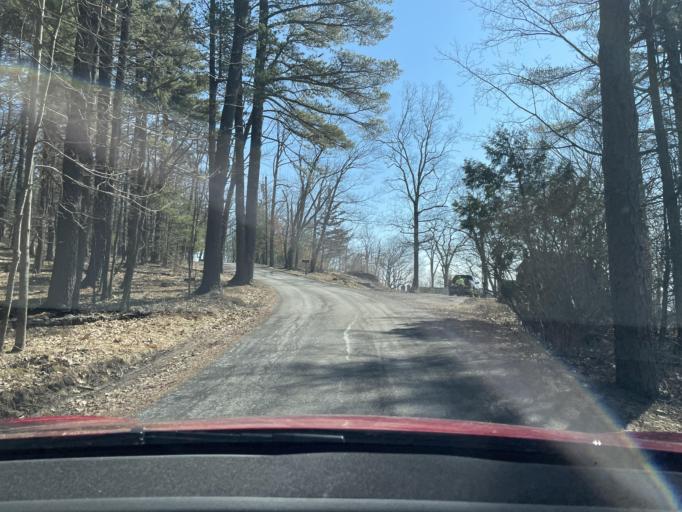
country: US
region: New York
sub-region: Ulster County
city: West Hurley
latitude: 42.0109
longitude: -74.1288
